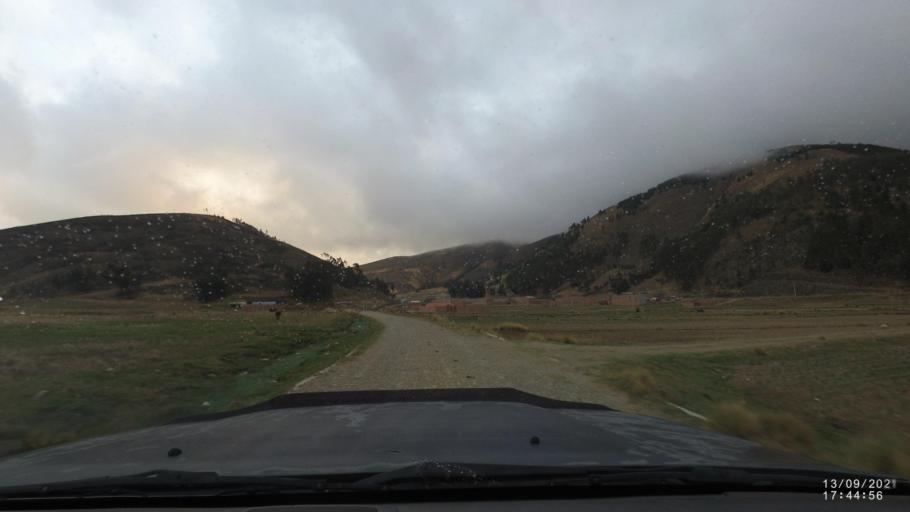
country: BO
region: Cochabamba
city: Colomi
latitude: -17.3744
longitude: -65.8311
